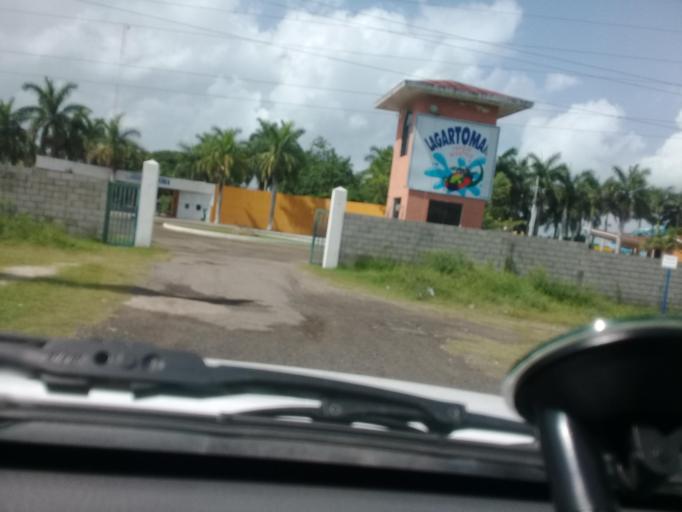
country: MX
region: Veracruz
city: Moralillo
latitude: 22.2127
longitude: -97.9726
